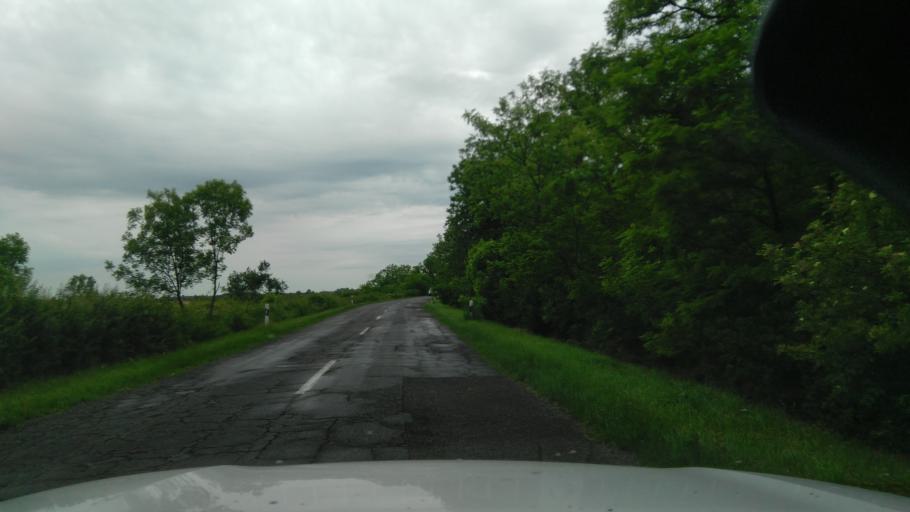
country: HU
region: Bekes
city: Bekescsaba
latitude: 46.6778
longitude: 21.1692
